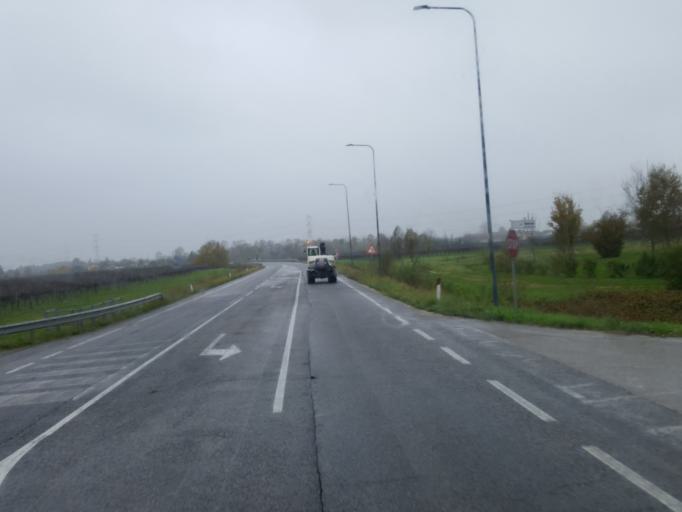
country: IT
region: Veneto
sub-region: Provincia di Treviso
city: Sambughe
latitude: 45.5718
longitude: 12.2206
